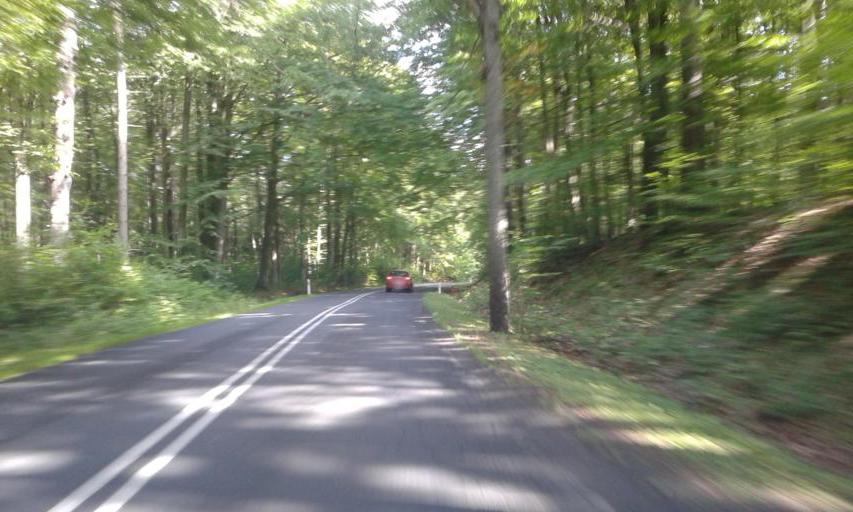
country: PL
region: West Pomeranian Voivodeship
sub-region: Powiat koszalinski
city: Polanow
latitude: 54.2333
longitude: 16.7018
